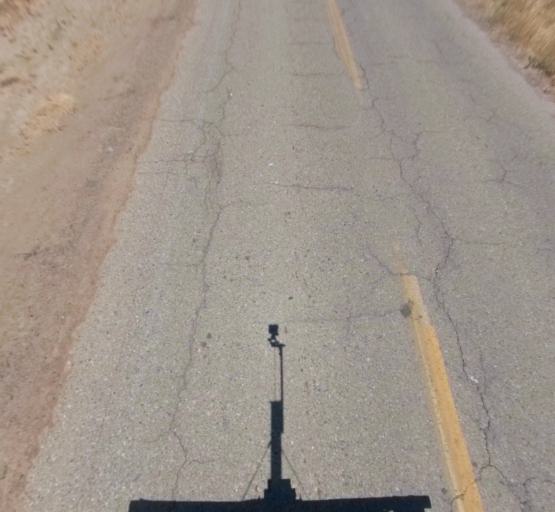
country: US
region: California
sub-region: Madera County
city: Parkwood
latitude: 36.8939
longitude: -120.1105
